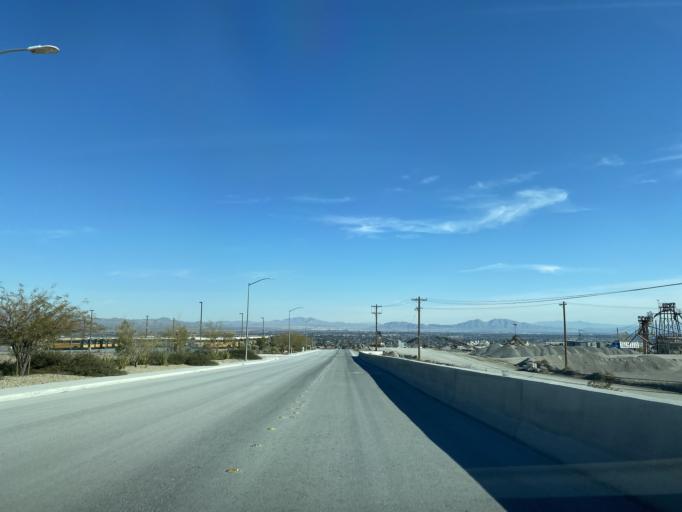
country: US
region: Nevada
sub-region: Clark County
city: Summerlin South
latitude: 36.2552
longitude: -115.3267
